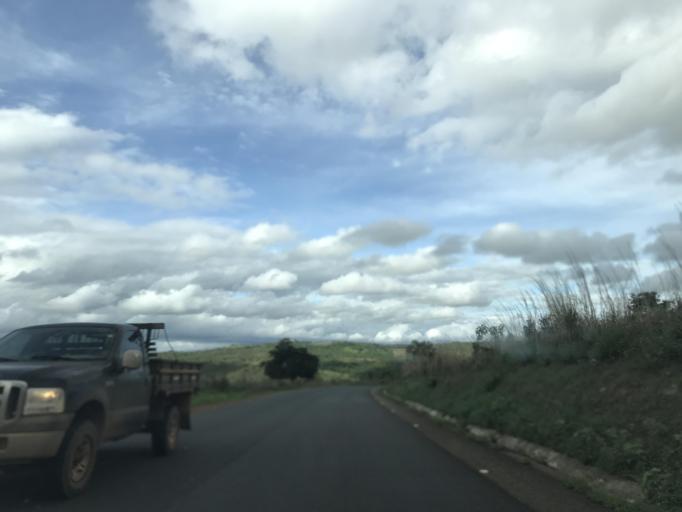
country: BR
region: Goias
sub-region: Vianopolis
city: Vianopolis
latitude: -16.9491
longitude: -48.5903
